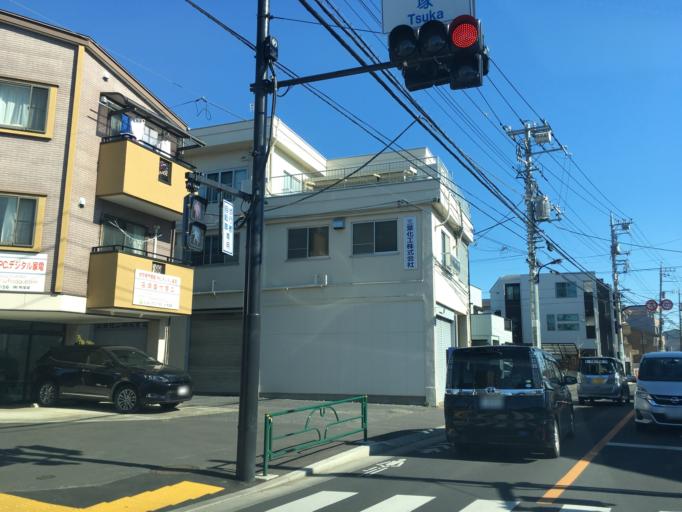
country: JP
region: Tokyo
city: Kamirenjaku
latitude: 35.6949
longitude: 139.5507
